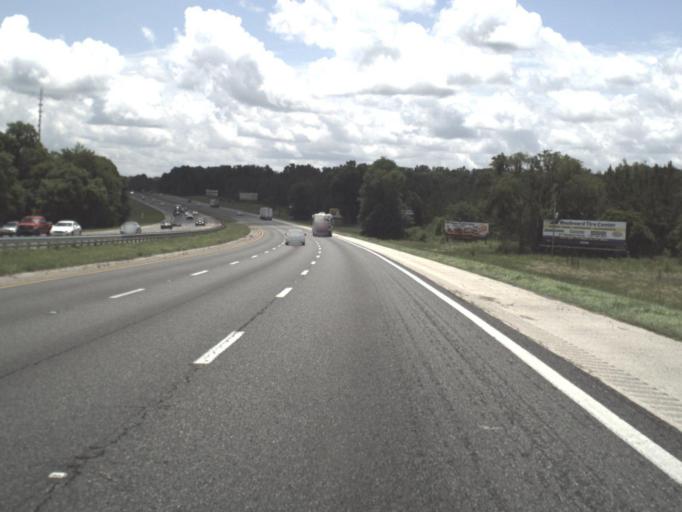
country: US
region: Florida
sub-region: Alachua County
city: Alachua
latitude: 29.7630
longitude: -82.5037
